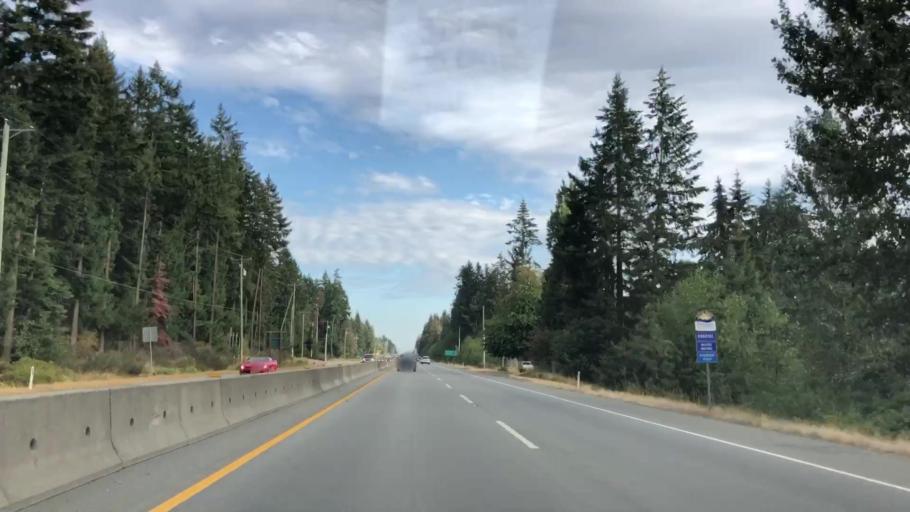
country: CA
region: British Columbia
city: Duncan
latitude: 48.7035
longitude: -123.6020
